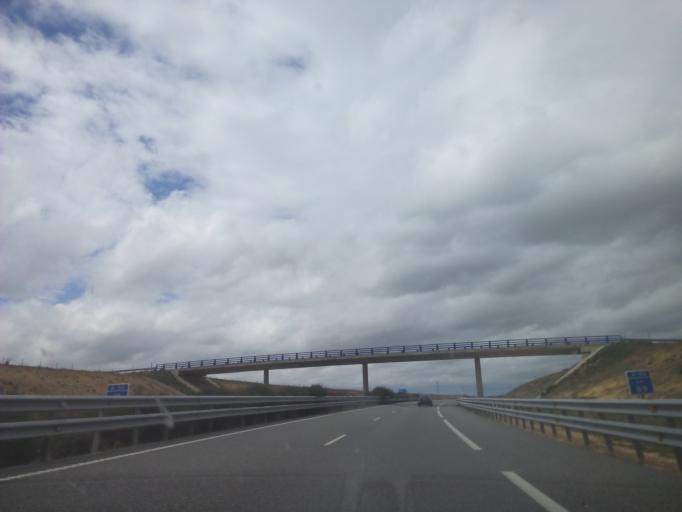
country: ES
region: Castille and Leon
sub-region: Provincia de Salamanca
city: Machacon
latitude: 40.9210
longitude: -5.5303
